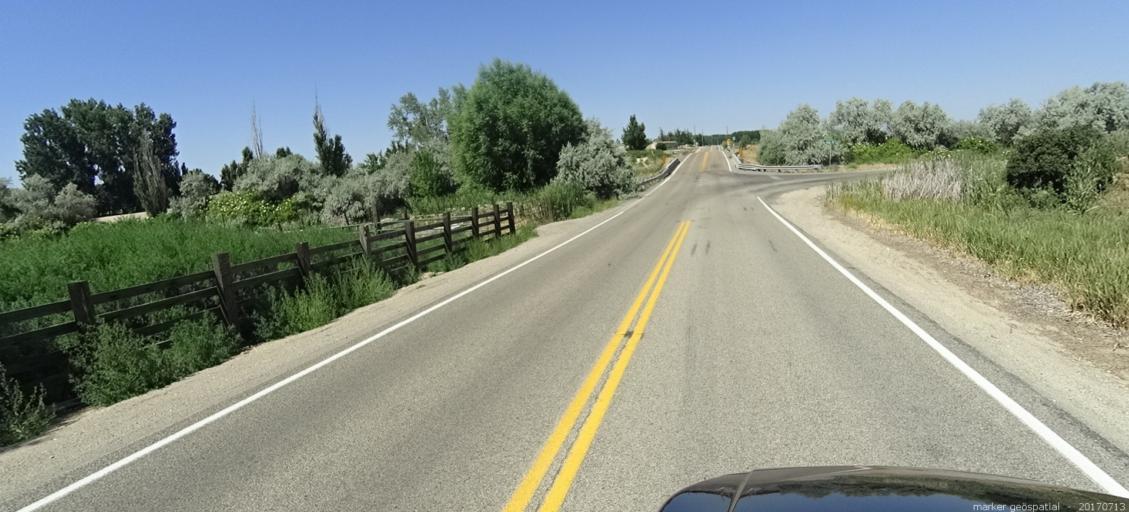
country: US
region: Idaho
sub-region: Ada County
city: Kuna
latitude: 43.5329
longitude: -116.4725
